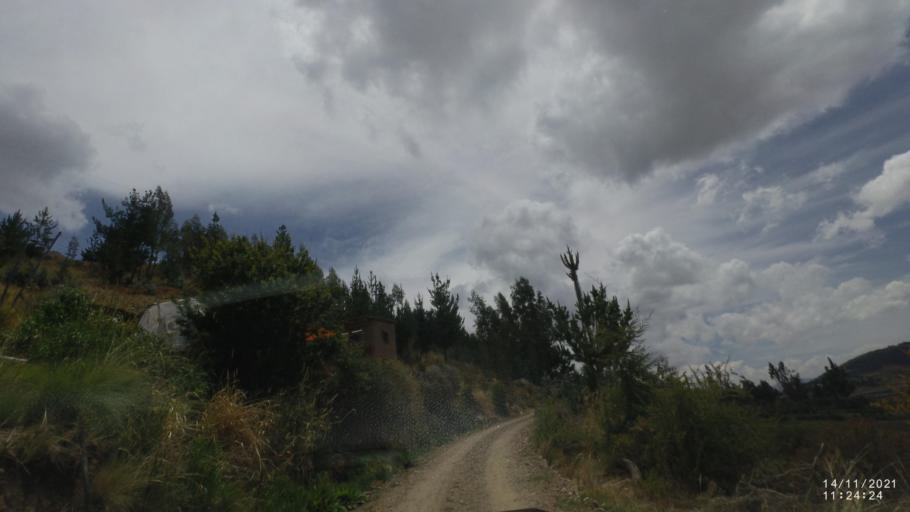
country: BO
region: Cochabamba
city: Cochabamba
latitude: -17.3343
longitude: -66.0262
